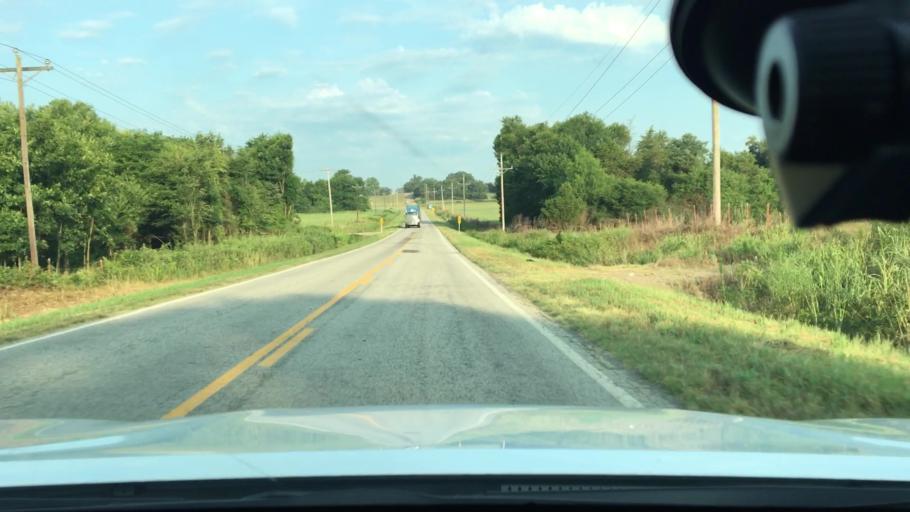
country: US
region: Arkansas
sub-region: Johnson County
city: Coal Hill
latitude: 35.3375
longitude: -93.6249
